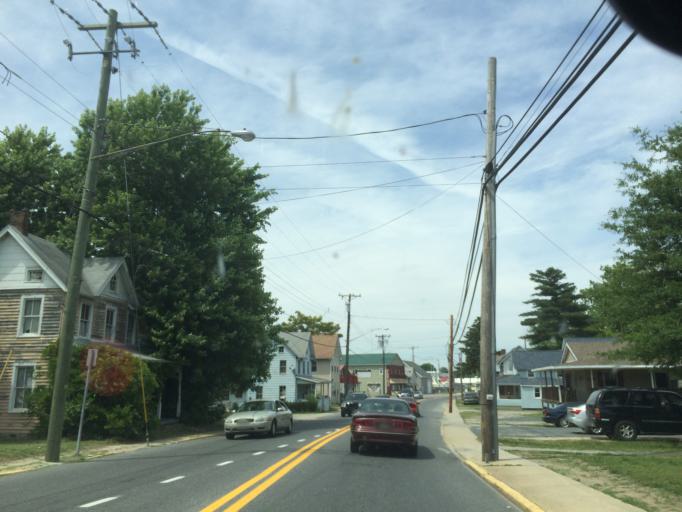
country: US
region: Delaware
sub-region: Sussex County
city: Blades
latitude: 38.6360
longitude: -75.6100
